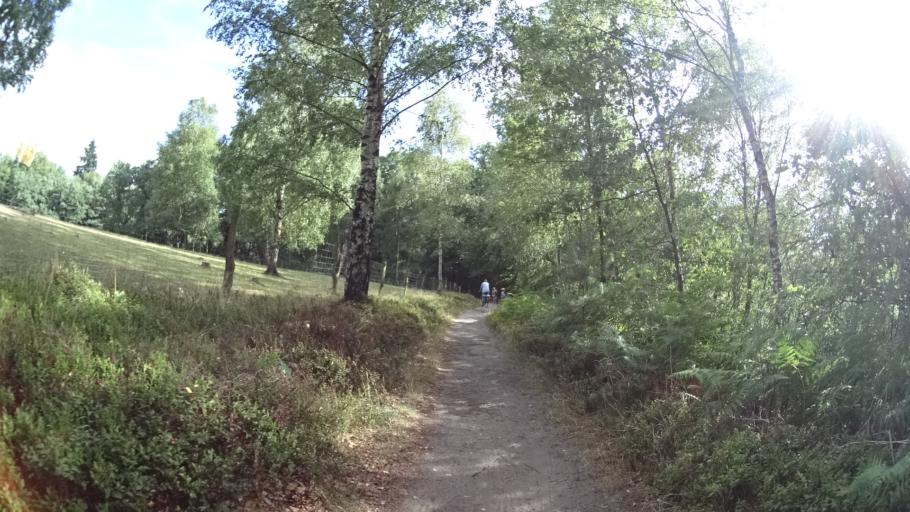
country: DE
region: Lower Saxony
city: Undeloh
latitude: 53.1548
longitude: 9.9238
